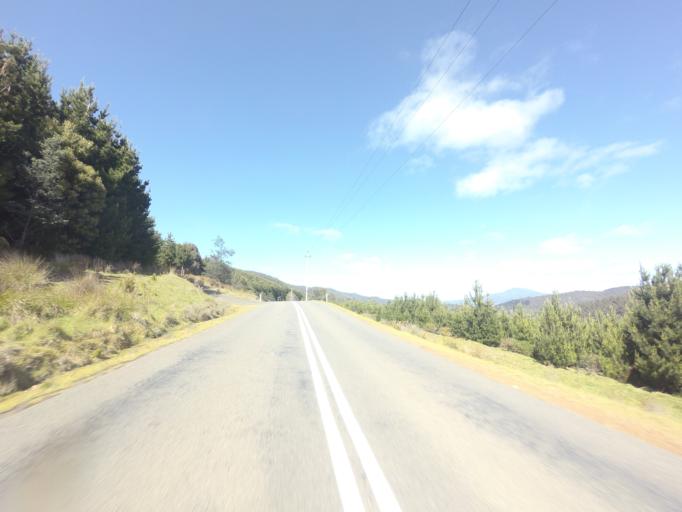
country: AU
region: Tasmania
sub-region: Derwent Valley
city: New Norfolk
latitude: -42.7418
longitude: 146.6577
